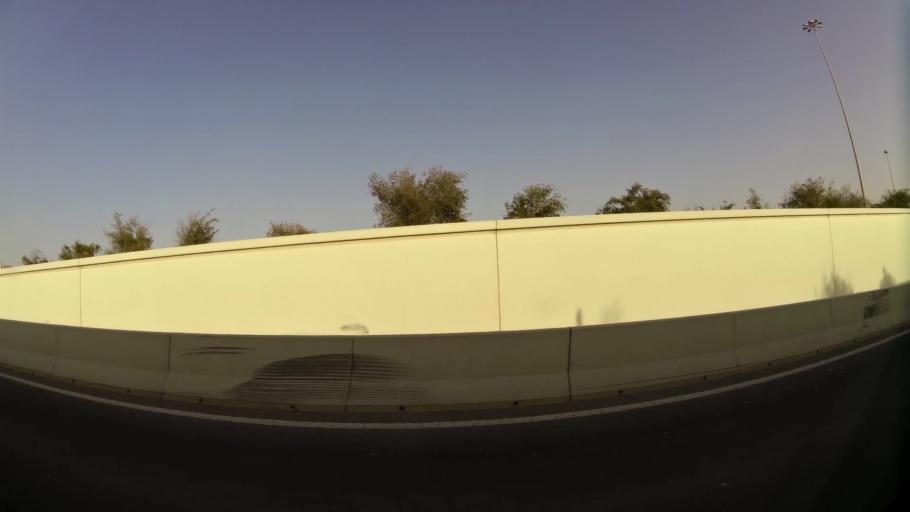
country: QA
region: Baladiyat ar Rayyan
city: Ar Rayyan
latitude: 25.3212
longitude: 51.4603
